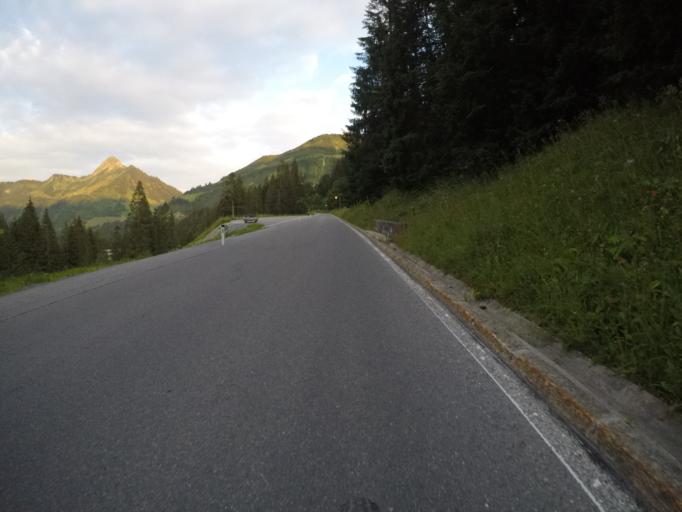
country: AT
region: Vorarlberg
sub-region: Politischer Bezirk Bregenz
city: Damuels
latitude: 47.2850
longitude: 9.8876
